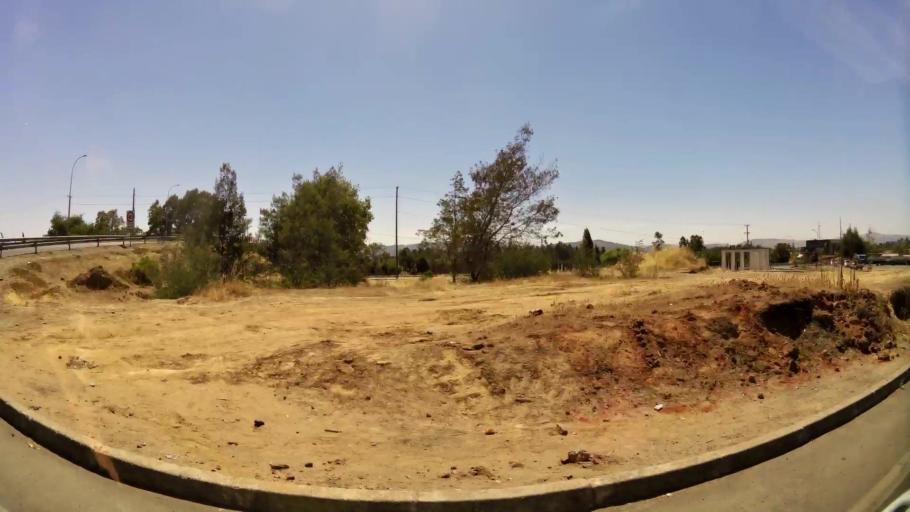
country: CL
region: Maule
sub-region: Provincia de Talca
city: Talca
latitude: -35.3037
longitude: -71.5174
